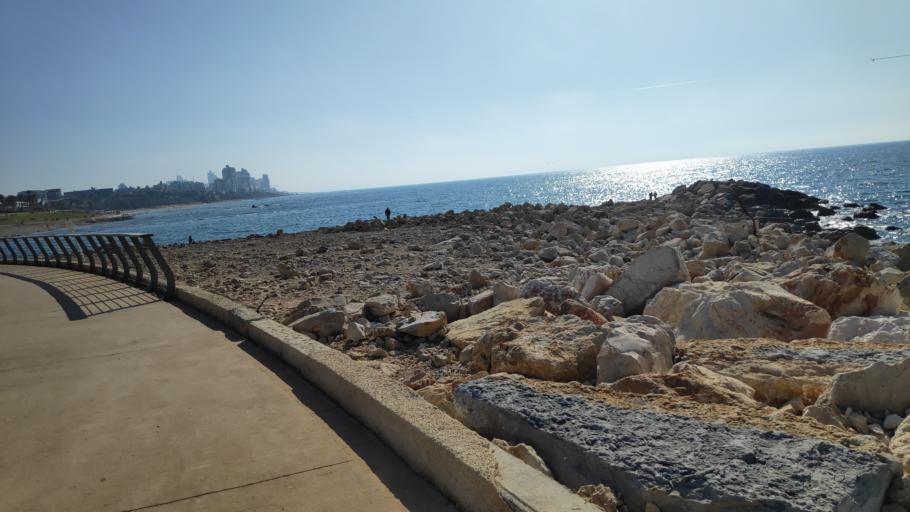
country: IL
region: Tel Aviv
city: Yafo
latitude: 32.0455
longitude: 34.7450
